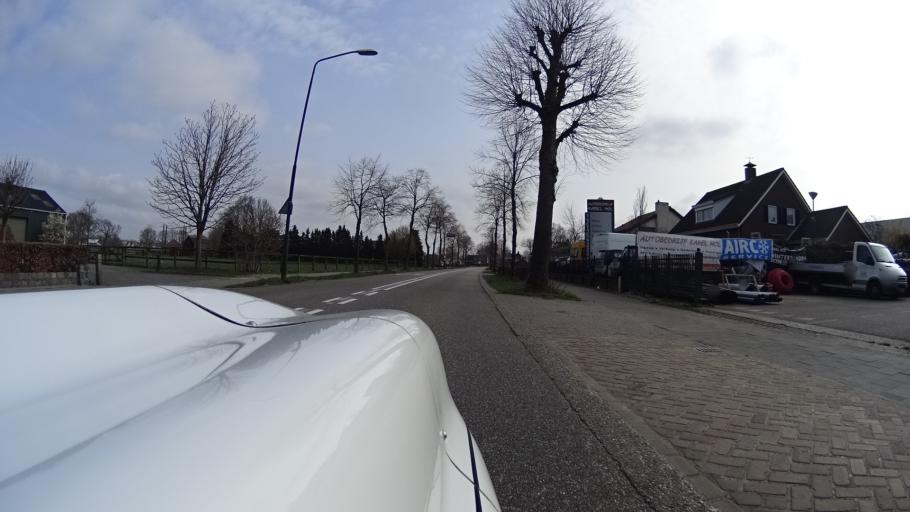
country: NL
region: North Brabant
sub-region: Gemeente Boekel
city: Boekel
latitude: 51.5441
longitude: 5.6958
